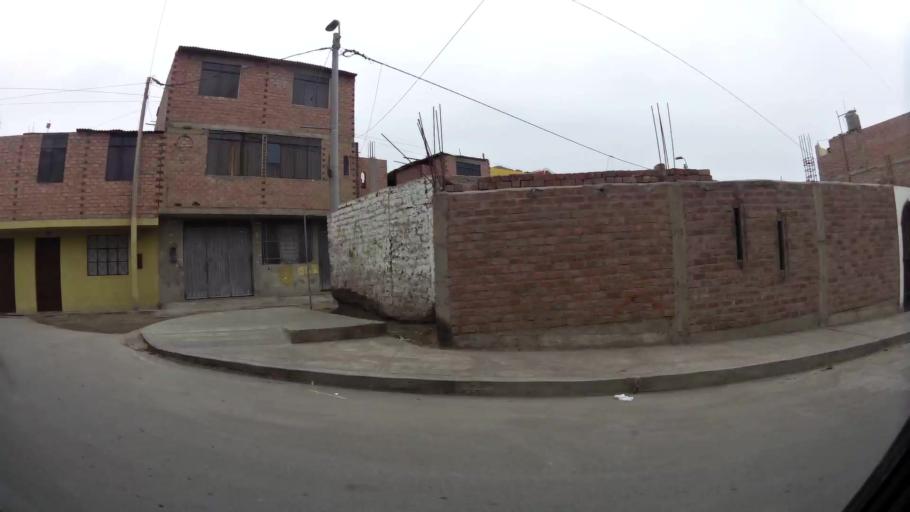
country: PE
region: Lima
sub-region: Barranca
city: Barranca
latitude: -10.7474
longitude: -77.7516
